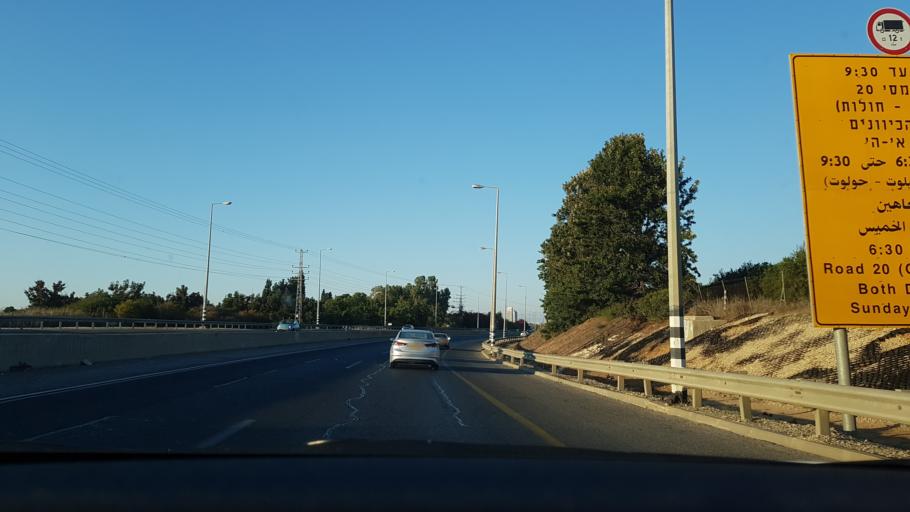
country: IL
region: Central District
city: Ness Ziona
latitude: 31.9410
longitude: 34.7800
